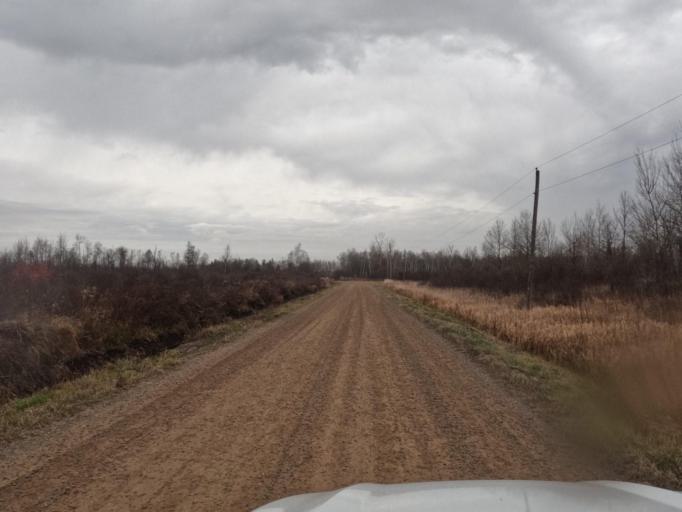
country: CA
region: Ontario
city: Shelburne
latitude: 43.8963
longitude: -80.3845
